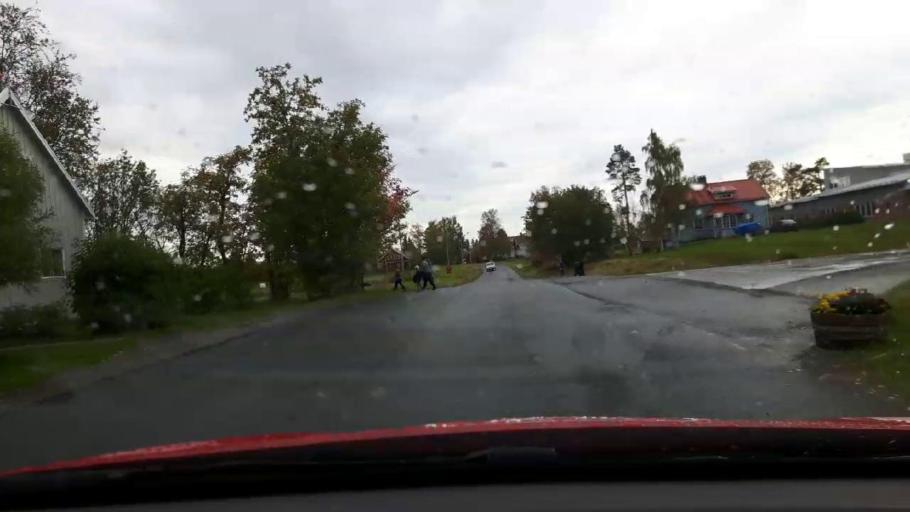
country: SE
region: Jaemtland
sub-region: Bergs Kommun
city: Hoverberg
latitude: 62.9225
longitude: 14.5165
